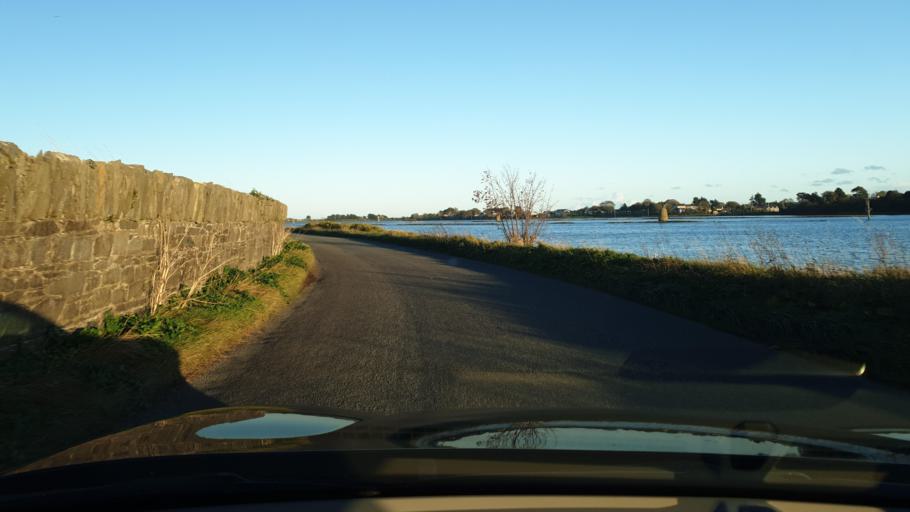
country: IE
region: Leinster
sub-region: Lu
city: Termonfeckin
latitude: 53.7243
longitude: -6.2944
